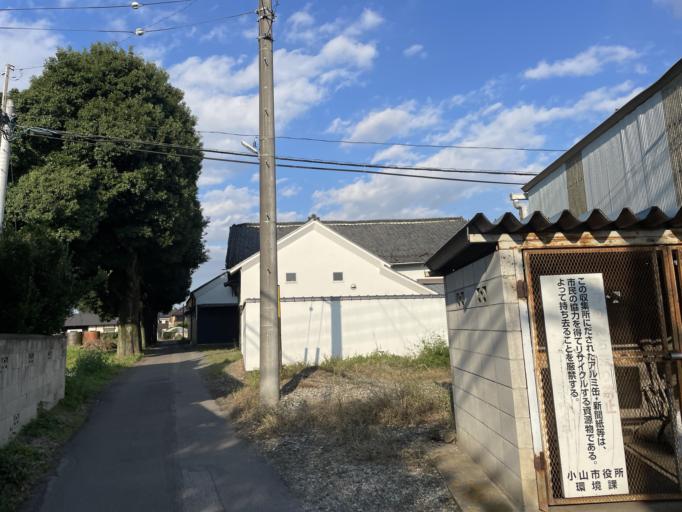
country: JP
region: Tochigi
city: Oyama
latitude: 36.2862
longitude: 139.7797
